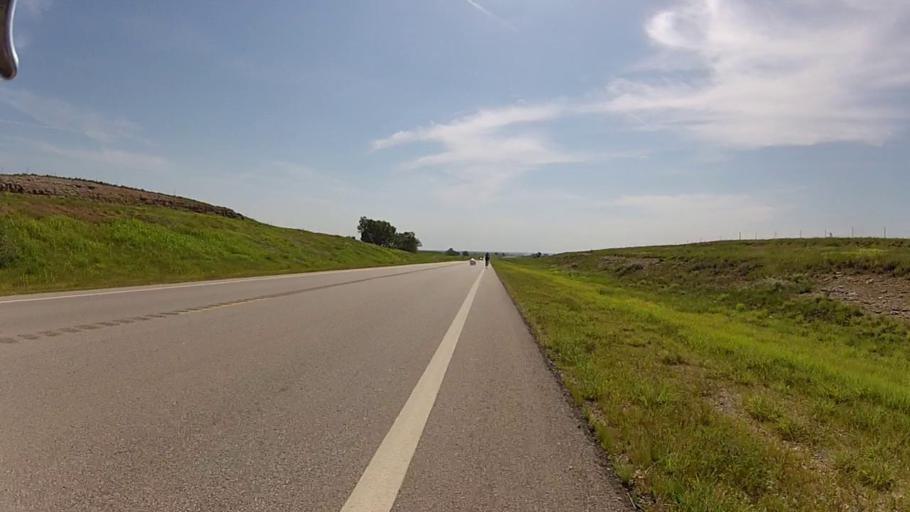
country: US
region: Kansas
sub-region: Cowley County
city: Winfield
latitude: 37.1108
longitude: -96.6324
